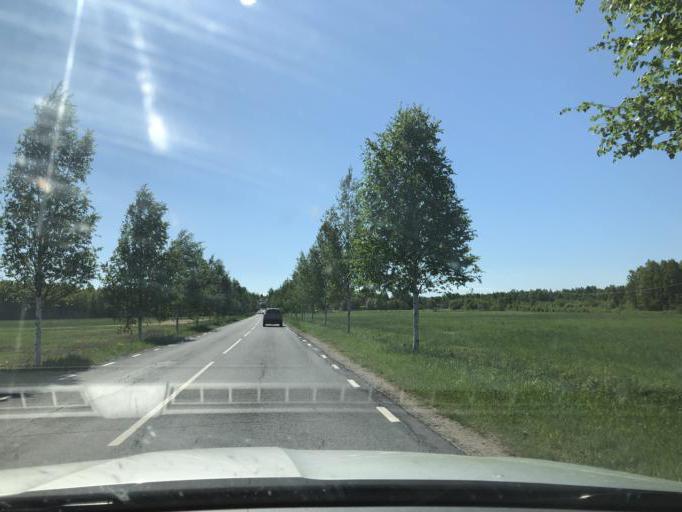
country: SE
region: Norrbotten
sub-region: Lulea Kommun
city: Gammelstad
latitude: 65.6515
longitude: 22.0180
